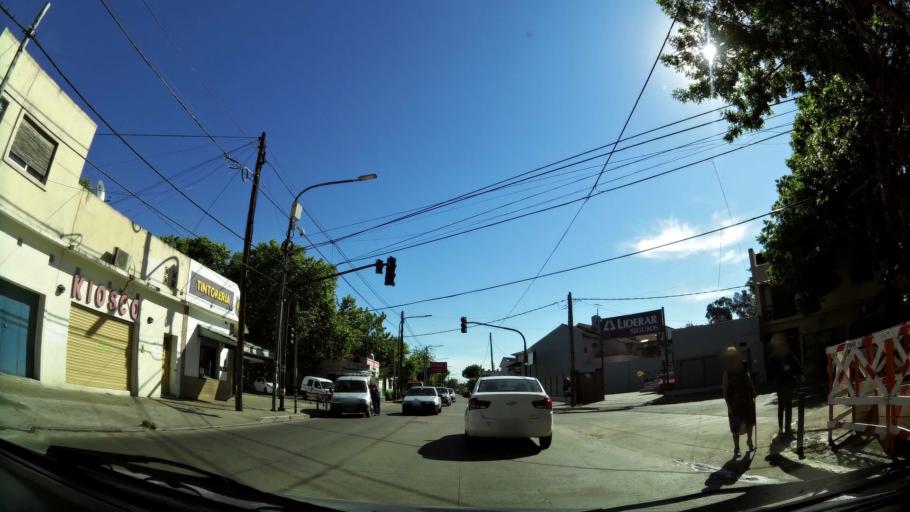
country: AR
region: Buenos Aires
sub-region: Partido de Lomas de Zamora
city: Lomas de Zamora
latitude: -34.7664
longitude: -58.4066
